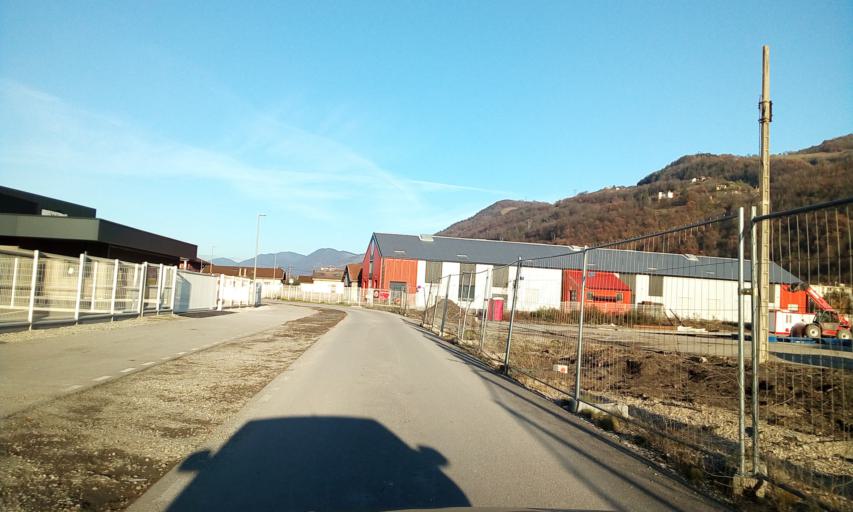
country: FR
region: Rhone-Alpes
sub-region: Departement de l'Isere
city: Villard-Bonnot
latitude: 45.2290
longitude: 5.8746
